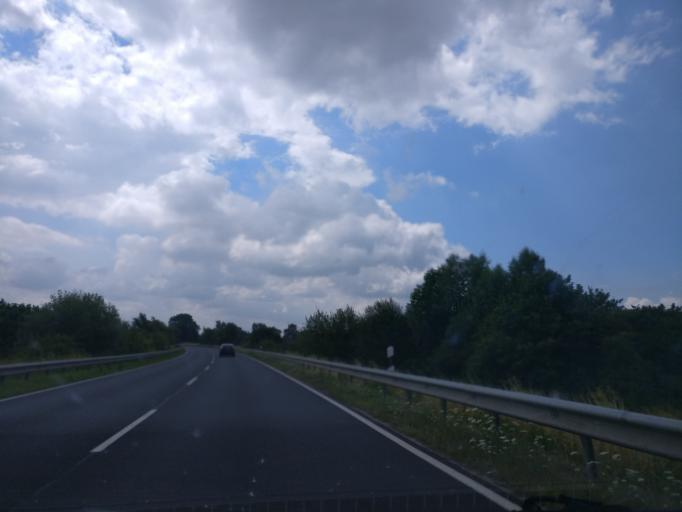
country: DE
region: Lower Saxony
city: Einbeck
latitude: 51.8319
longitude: 9.8314
